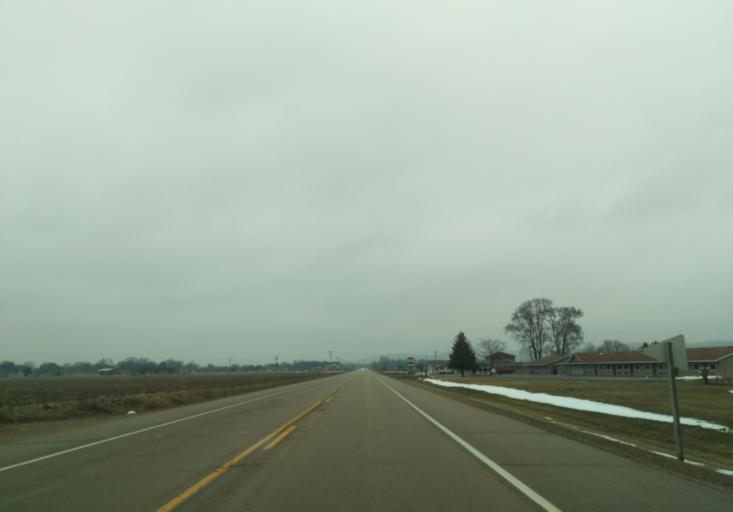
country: US
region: Wisconsin
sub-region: Sauk County
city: Spring Green
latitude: 43.1775
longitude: -90.0531
